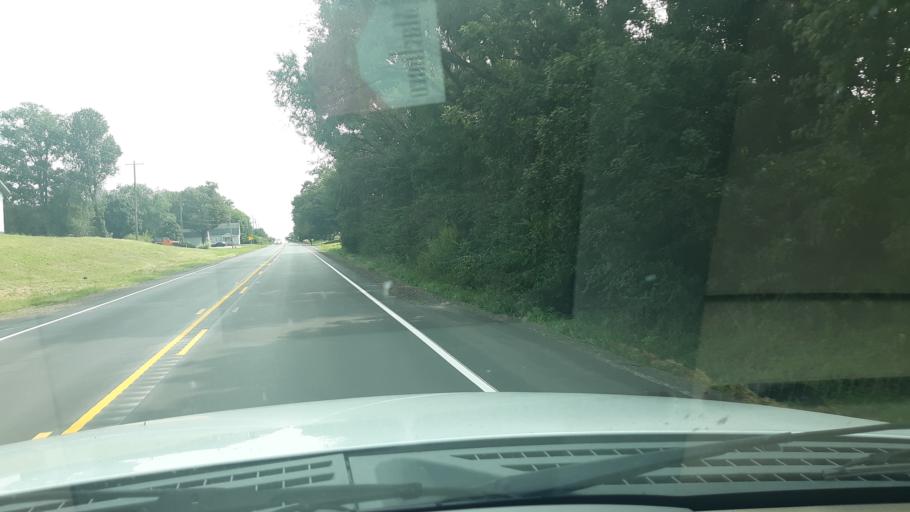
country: US
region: Indiana
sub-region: Gibson County
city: Princeton
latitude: 38.3556
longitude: -87.6218
